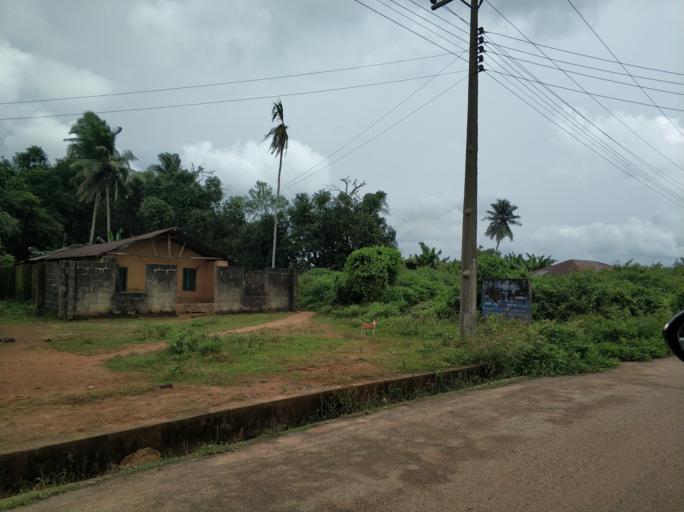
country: NG
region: Ogun
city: Abigi
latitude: 6.6131
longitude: 4.5442
